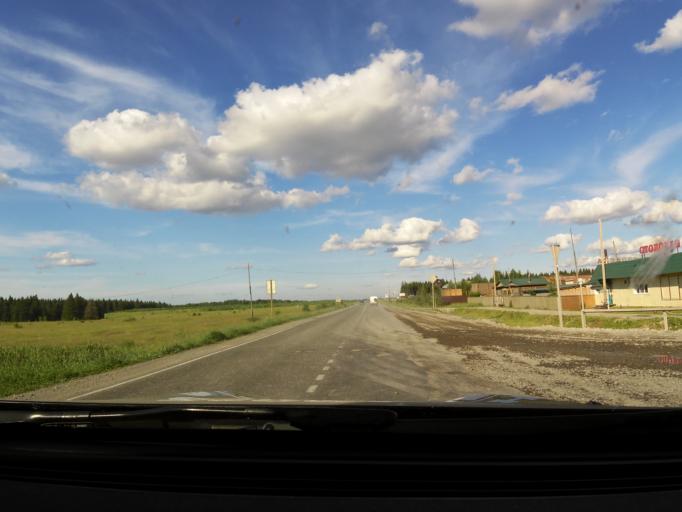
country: RU
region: Kirov
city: Omutninsk
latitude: 58.6873
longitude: 52.1560
